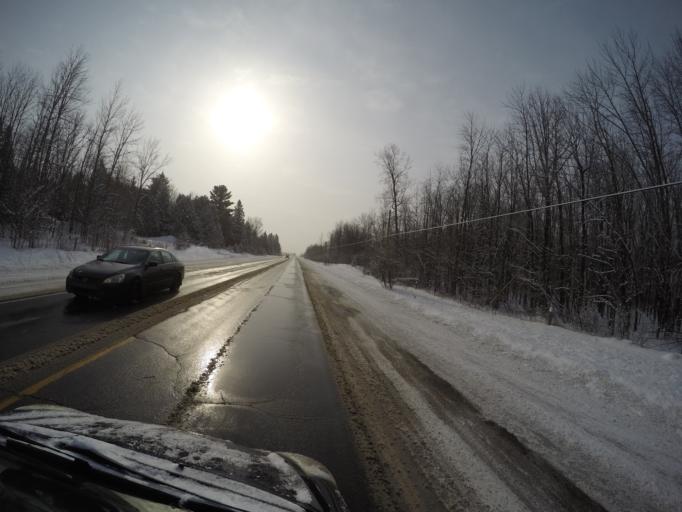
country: CA
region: Ontario
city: Clarence-Rockland
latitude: 45.4334
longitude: -75.4144
